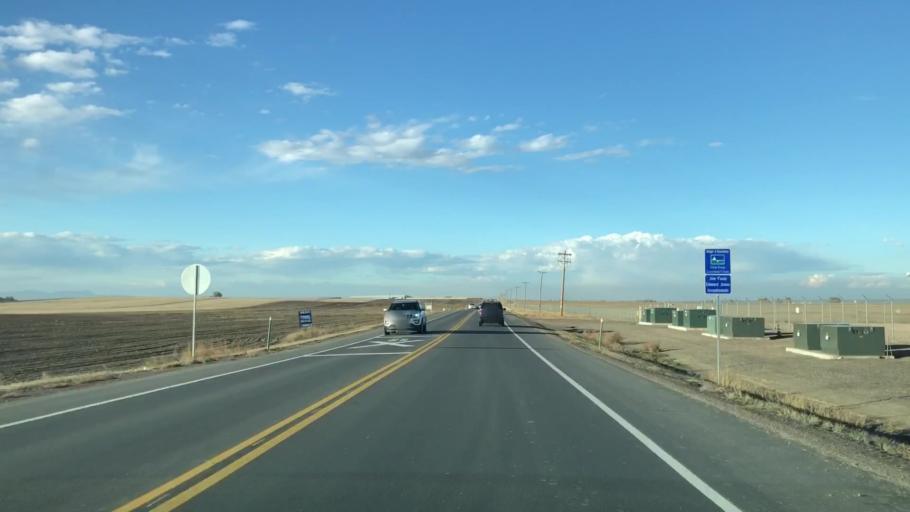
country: US
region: Colorado
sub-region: Larimer County
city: Loveland
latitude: 40.4466
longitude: -105.0204
